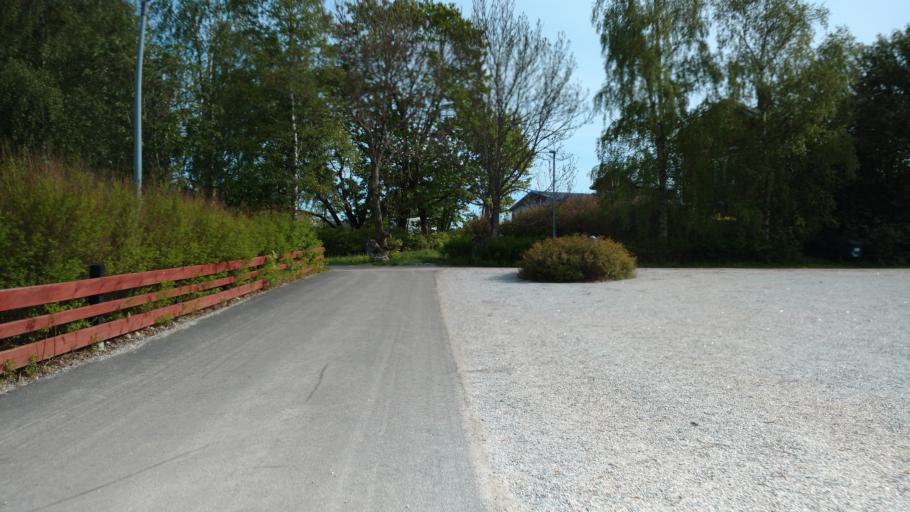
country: FI
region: Varsinais-Suomi
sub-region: Salo
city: Salo
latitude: 60.3806
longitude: 23.1457
